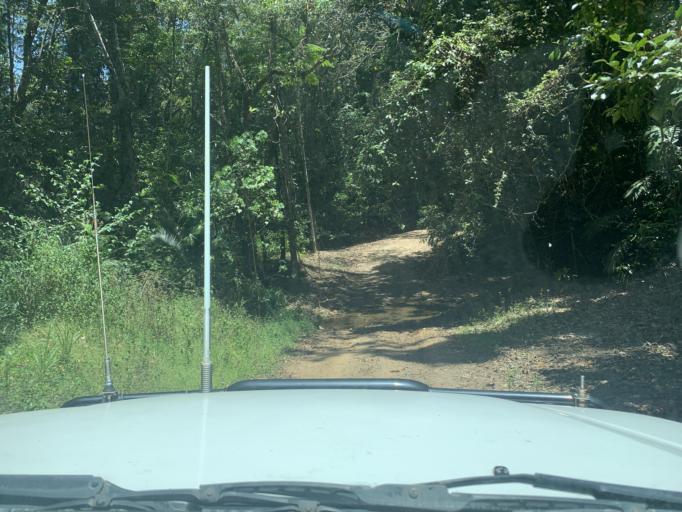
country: AU
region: Queensland
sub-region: Cairns
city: Redlynch
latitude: -16.9530
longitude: 145.6368
